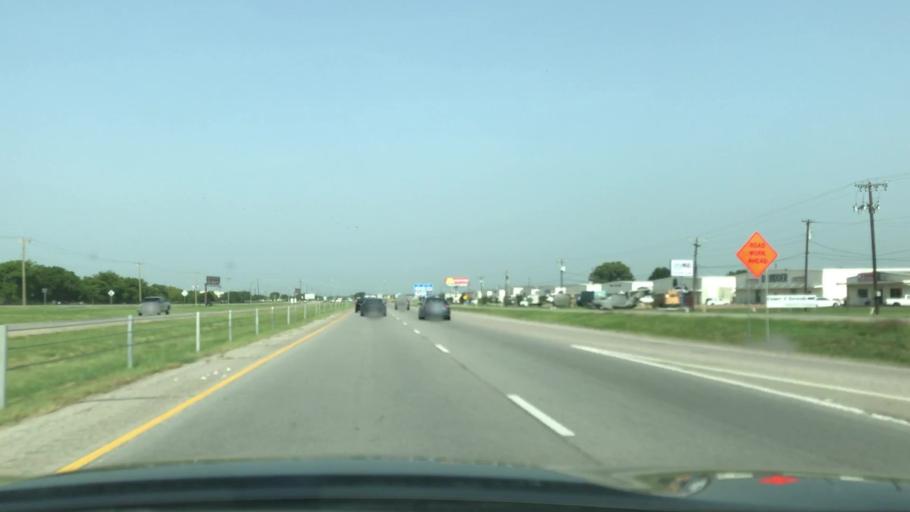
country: US
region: Texas
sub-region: Kaufman County
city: Forney
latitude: 32.7412
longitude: -96.4345
